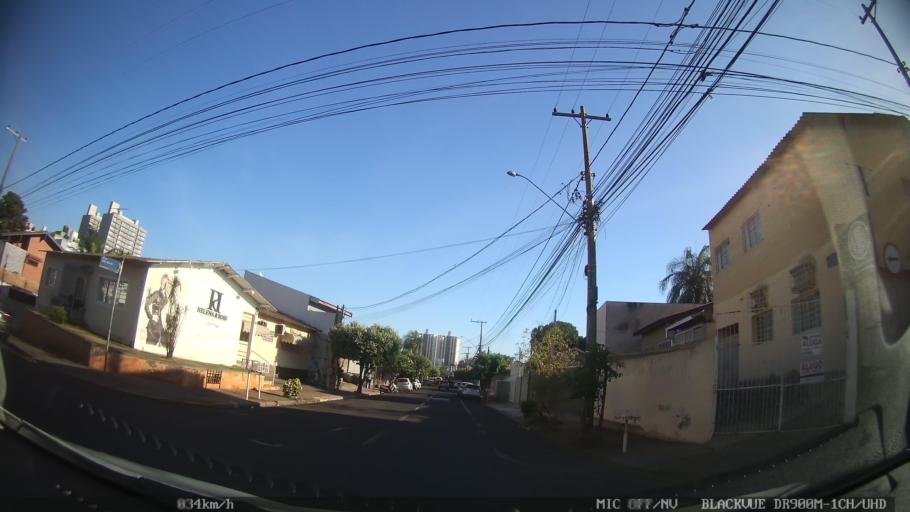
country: BR
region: Sao Paulo
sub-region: Sao Jose Do Rio Preto
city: Sao Jose do Rio Preto
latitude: -20.8158
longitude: -49.3949
